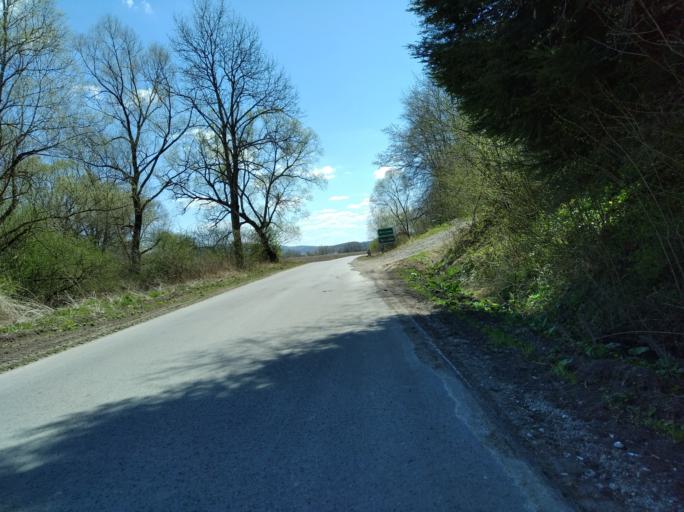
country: PL
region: Subcarpathian Voivodeship
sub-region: Powiat brzozowski
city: Dydnia
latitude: 49.6835
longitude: 22.2401
